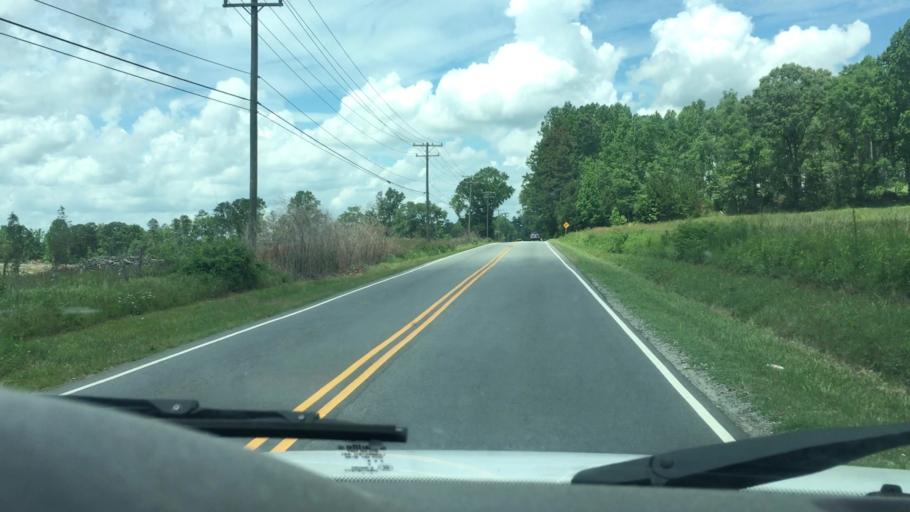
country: US
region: North Carolina
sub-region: Mecklenburg County
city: Huntersville
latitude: 35.4193
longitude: -80.7483
